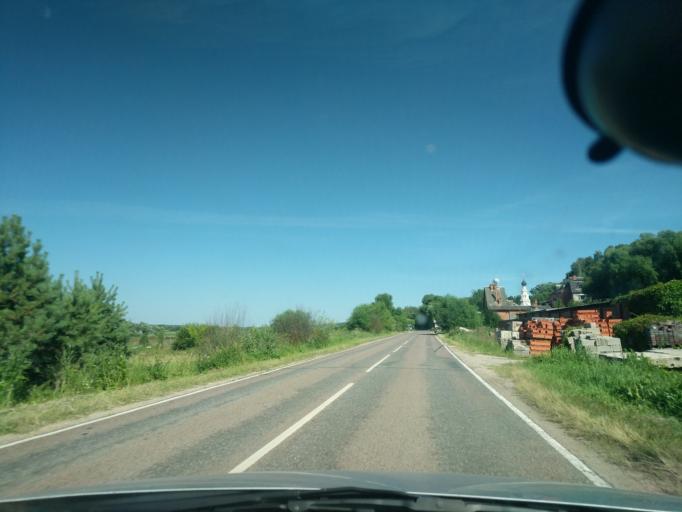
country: RU
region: Moskovskaya
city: Pushchino
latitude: 54.8426
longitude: 37.5442
